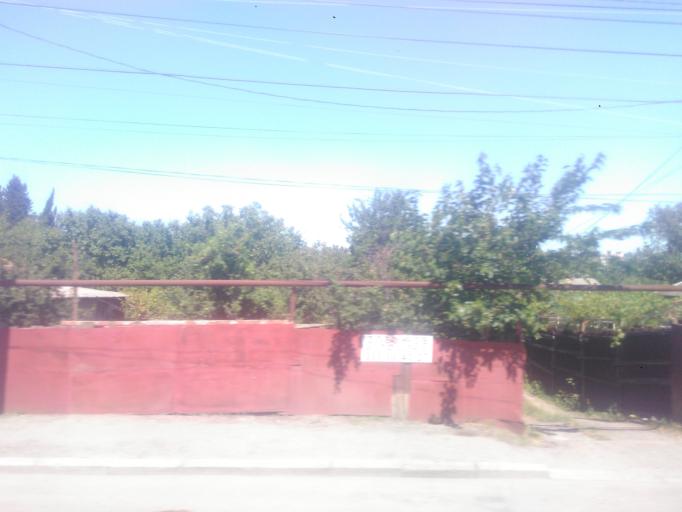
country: GE
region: T'bilisi
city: Tbilisi
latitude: 41.6974
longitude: 44.8892
